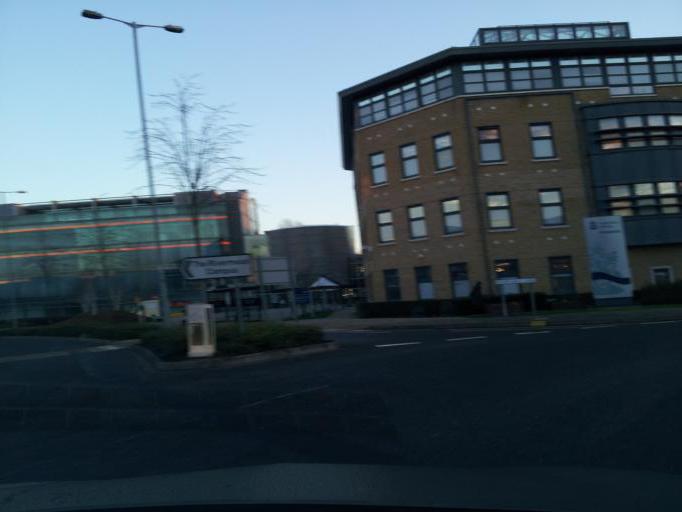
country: GB
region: England
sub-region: Essex
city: Chelmsford
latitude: 51.7408
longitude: 0.4736
